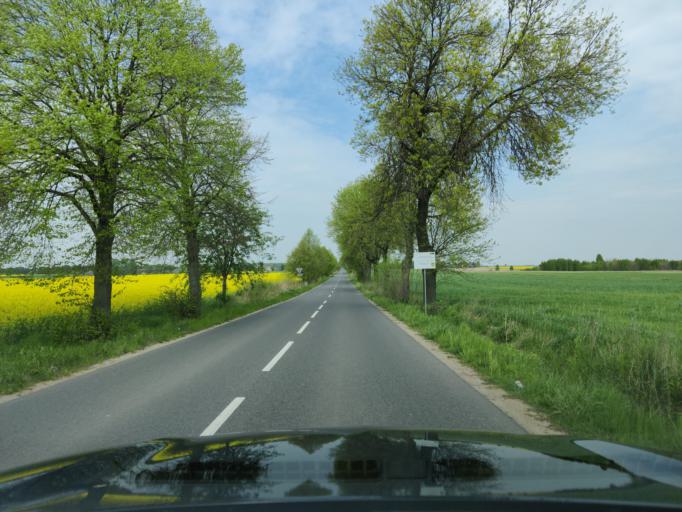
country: PL
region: Masovian Voivodeship
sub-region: Powiat pultuski
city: Zatory
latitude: 52.5506
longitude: 21.1883
